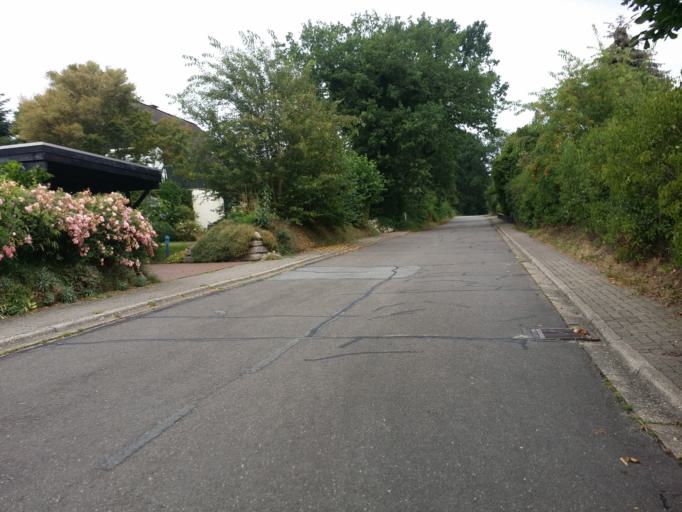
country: DE
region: Schleswig-Holstein
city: Oldendorf
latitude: 53.9464
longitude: 9.4599
